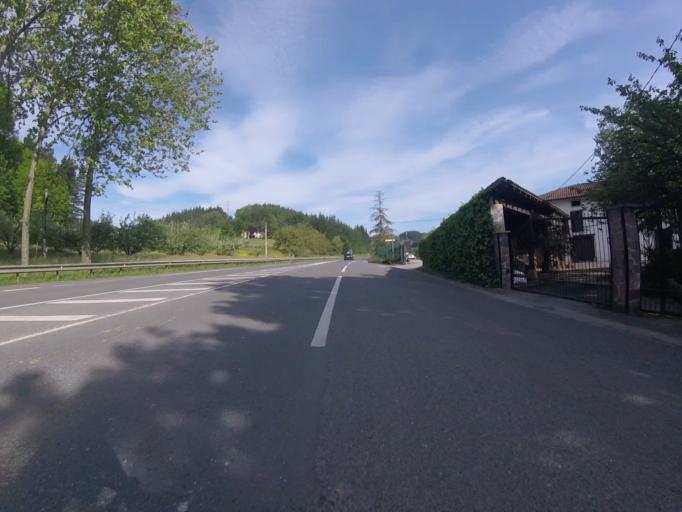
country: ES
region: Basque Country
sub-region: Provincia de Guipuzcoa
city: Ormaiztegui
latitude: 43.0548
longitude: -2.2656
